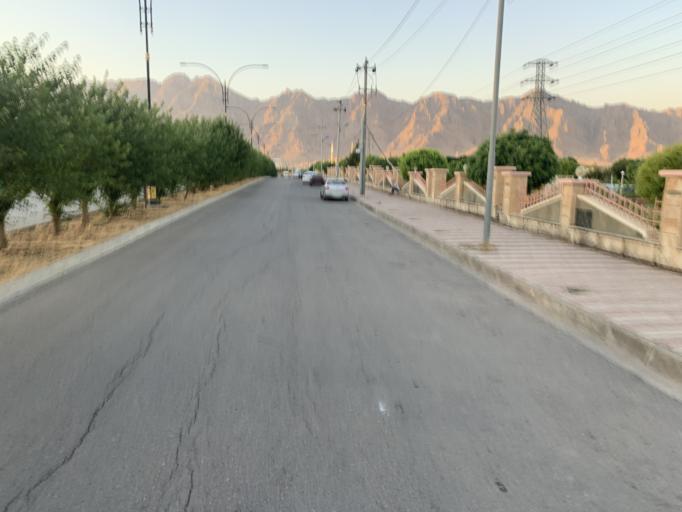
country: IQ
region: As Sulaymaniyah
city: Raniye
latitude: 36.2432
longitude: 44.8767
